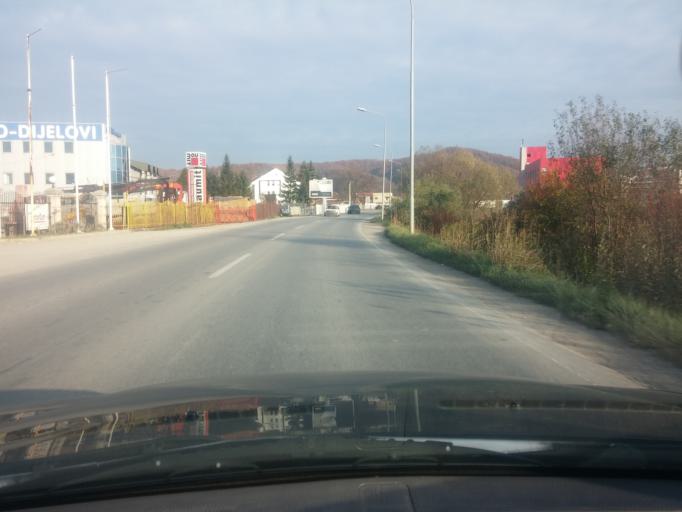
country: BA
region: Republika Srpska
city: Banja Luka
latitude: 44.8187
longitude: 17.2070
